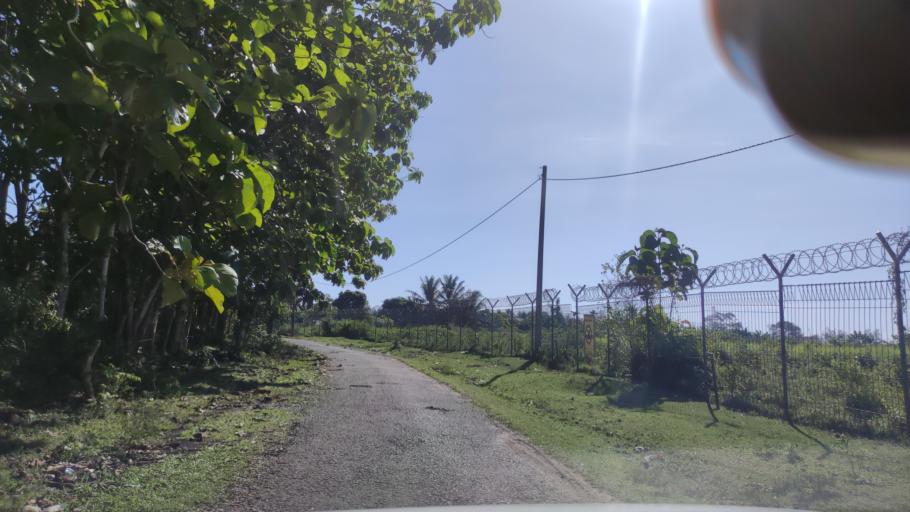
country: ID
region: Jambi
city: Sungai Penuh
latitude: -2.5479
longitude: 101.0880
